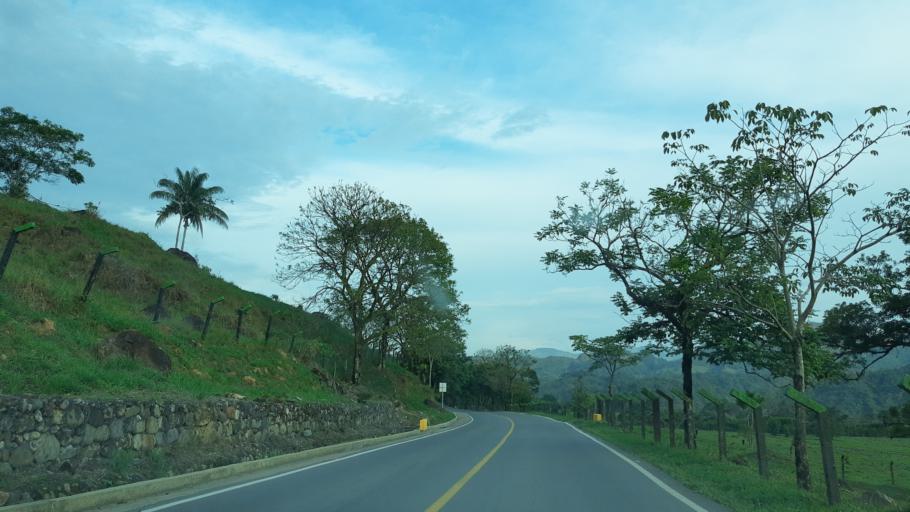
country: CO
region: Boyaca
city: San Luis de Gaceno
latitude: 4.8248
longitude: -73.2014
